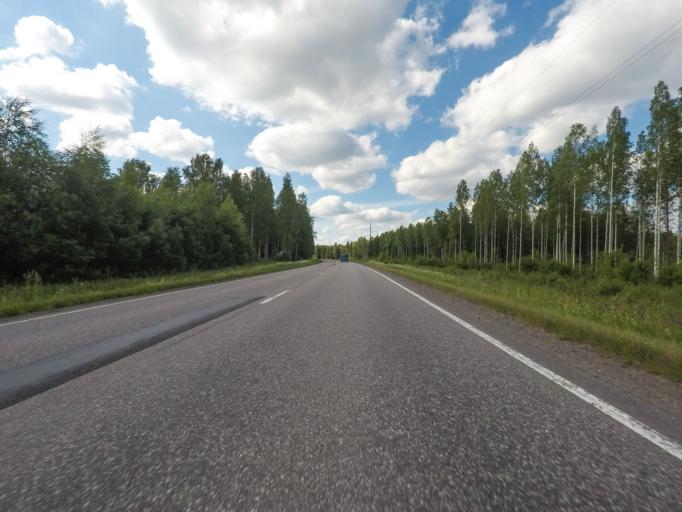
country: FI
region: Southern Savonia
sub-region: Savonlinna
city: Kerimaeki
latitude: 61.8393
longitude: 29.2163
